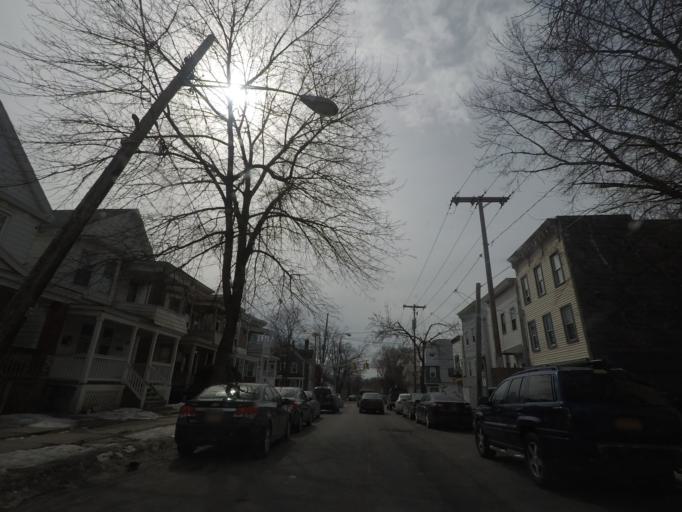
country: US
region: New York
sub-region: Albany County
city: West Albany
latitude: 42.6600
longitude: -73.7828
